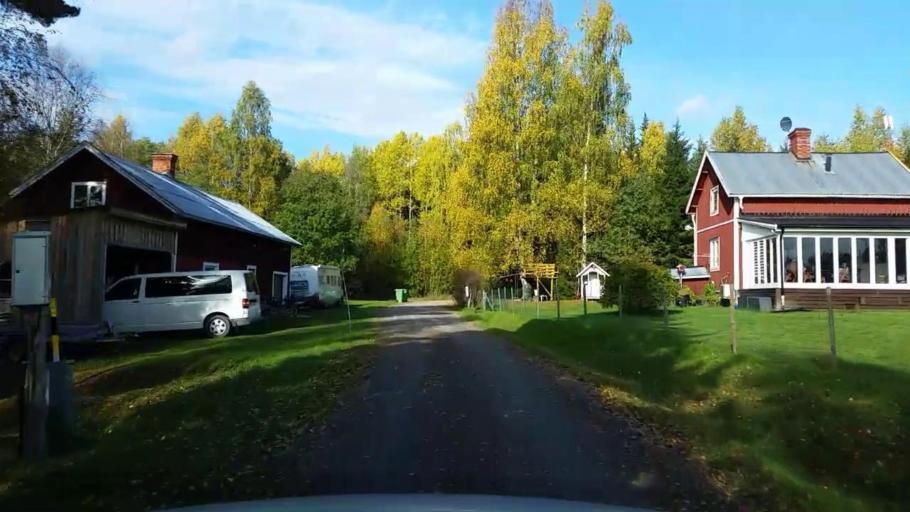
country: SE
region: Gaevleborg
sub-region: Ljusdals Kommun
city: Jaervsoe
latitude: 61.7865
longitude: 16.1523
